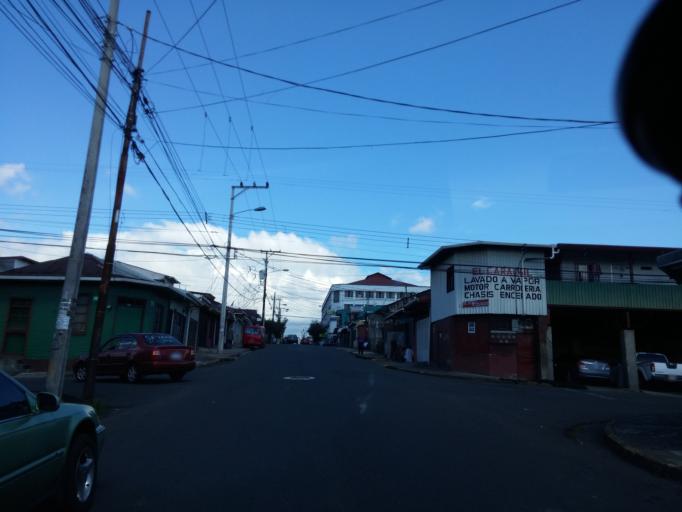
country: CR
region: San Jose
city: San Jose
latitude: 9.9242
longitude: -84.0845
